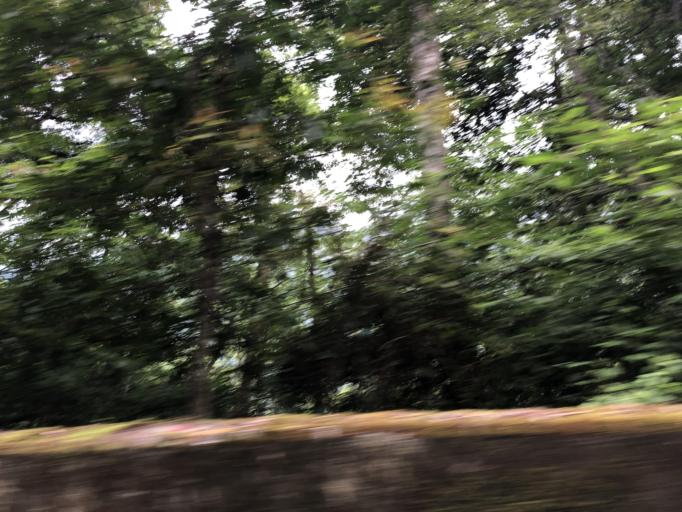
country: TW
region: Taiwan
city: Daxi
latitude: 24.7072
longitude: 121.4243
